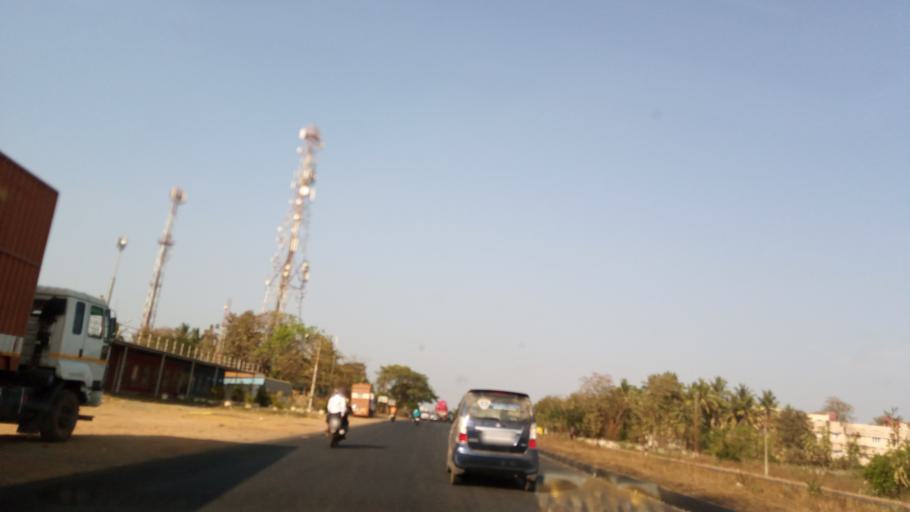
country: IN
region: Tamil Nadu
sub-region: Kancheepuram
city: Nandambakkam
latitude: 13.0289
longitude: 80.0308
